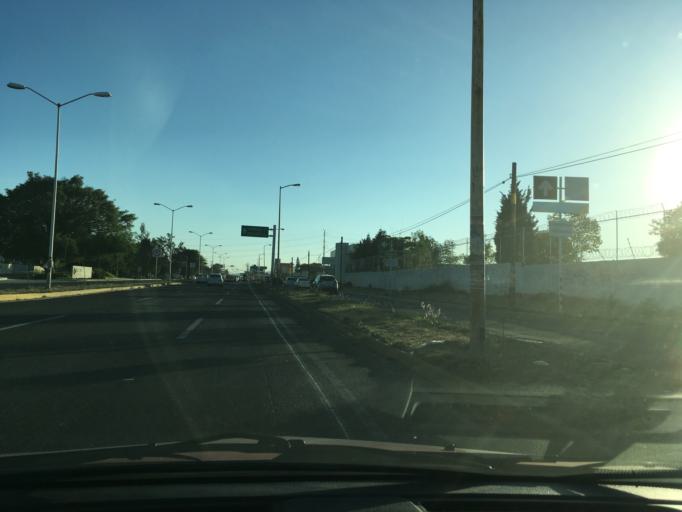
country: MX
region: Jalisco
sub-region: Tlajomulco de Zuniga
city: La Tijera
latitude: 20.5732
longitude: -103.4370
